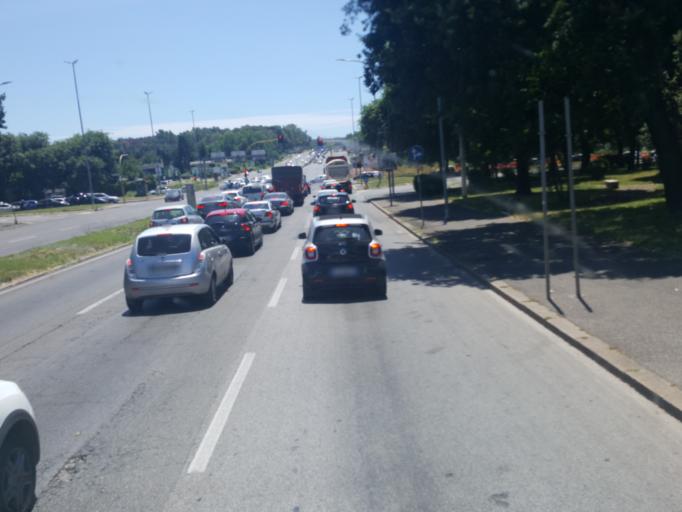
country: IT
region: Latium
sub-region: Citta metropolitana di Roma Capitale
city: Selcetta
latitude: 41.8195
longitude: 12.4634
